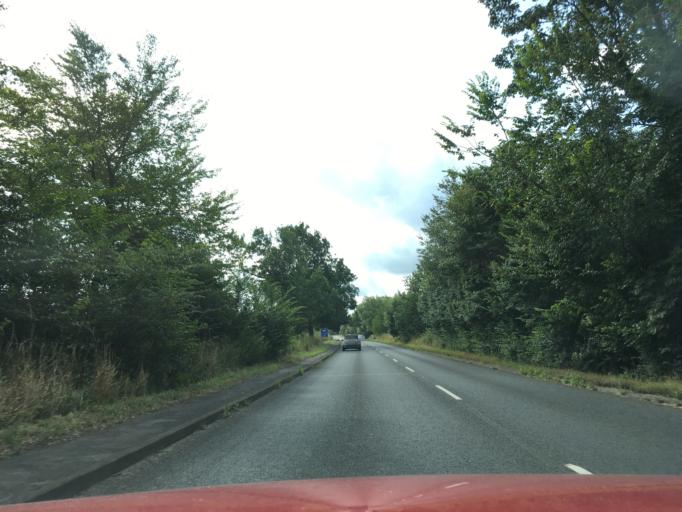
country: GB
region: England
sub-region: Hampshire
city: Bishops Waltham
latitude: 50.9632
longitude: -1.2371
